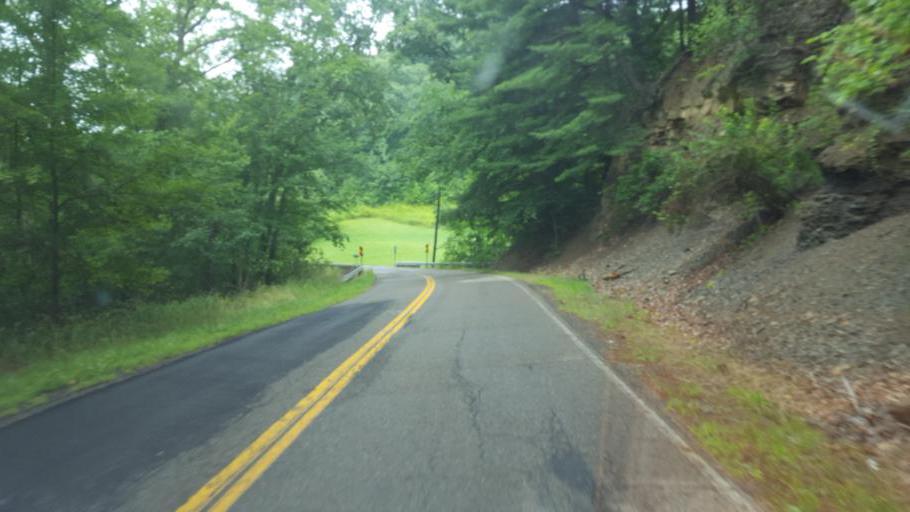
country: US
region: Ohio
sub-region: Columbiana County
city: Salineville
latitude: 40.5315
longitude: -80.8170
